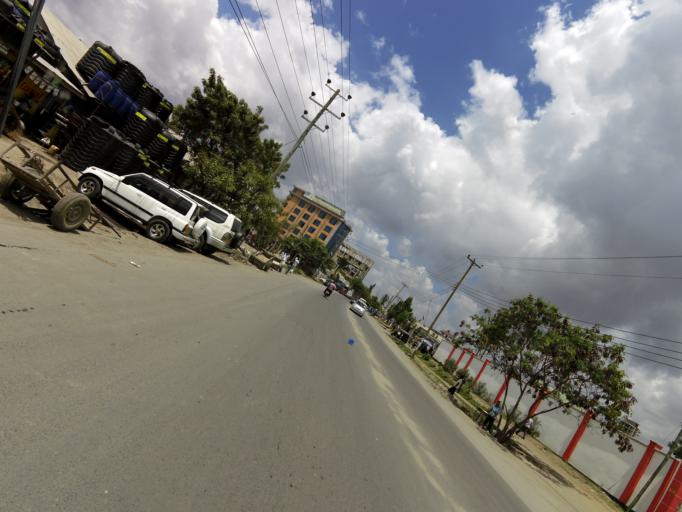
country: TZ
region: Dar es Salaam
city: Magomeni
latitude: -6.7869
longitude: 39.2229
